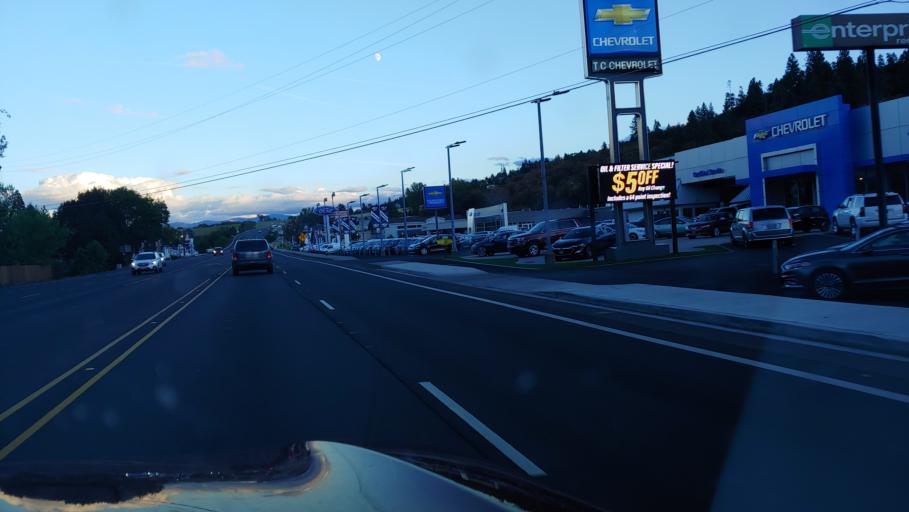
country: US
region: Oregon
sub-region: Jackson County
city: Ashland
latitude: 42.2204
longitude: -122.7400
